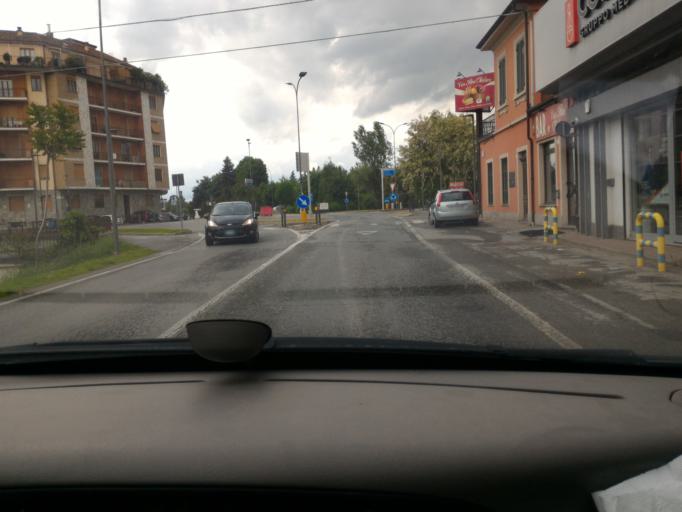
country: IT
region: Piedmont
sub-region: Provincia di Cuneo
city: Savigliano
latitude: 44.6487
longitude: 7.6509
